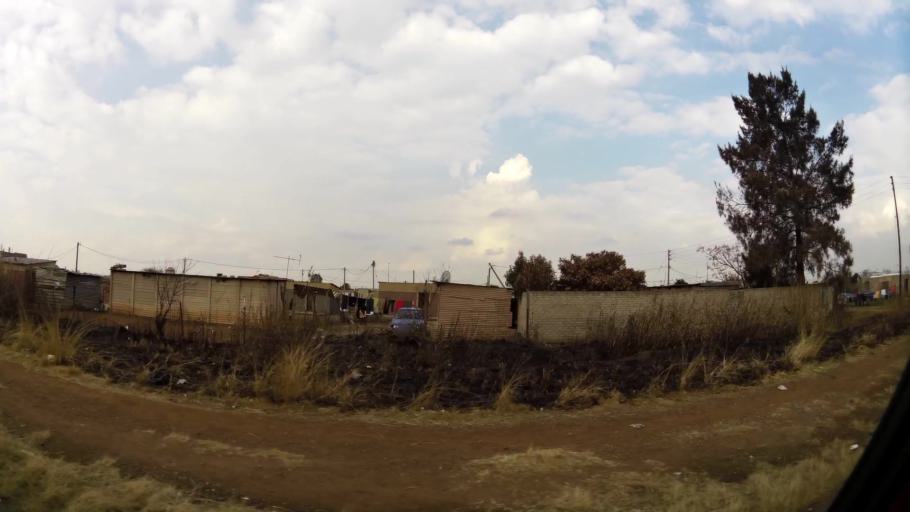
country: ZA
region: Gauteng
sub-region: Sedibeng District Municipality
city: Vanderbijlpark
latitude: -26.6732
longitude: 27.8598
